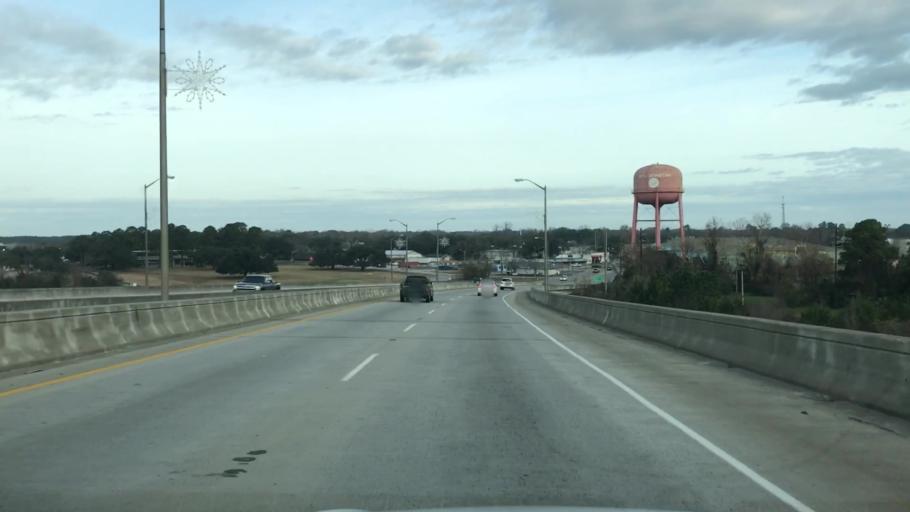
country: US
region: South Carolina
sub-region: Georgetown County
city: Georgetown
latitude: 33.3607
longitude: -79.2950
